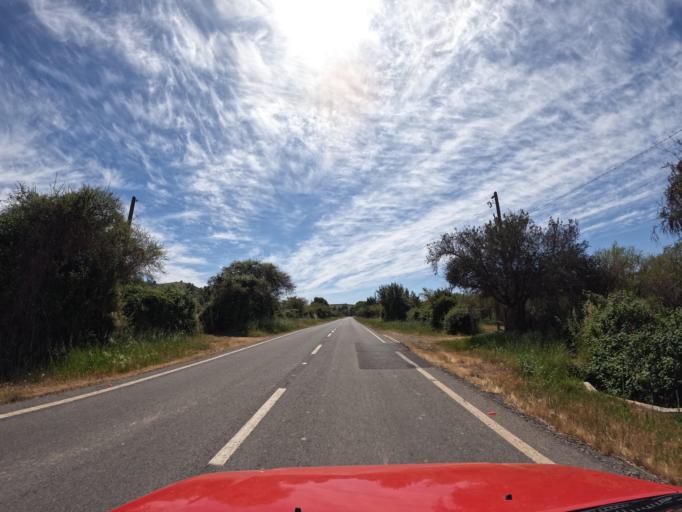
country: CL
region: Maule
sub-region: Provincia de Talca
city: Talca
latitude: -35.0293
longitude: -71.7644
